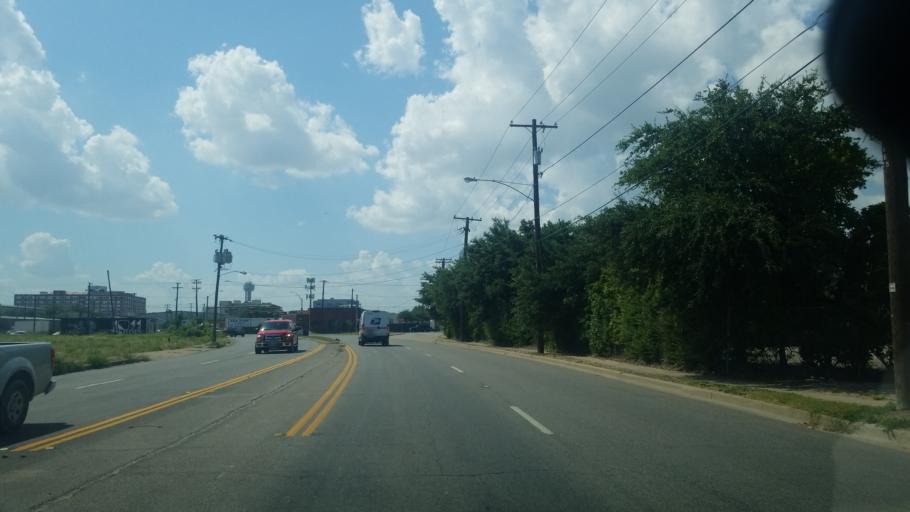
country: US
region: Texas
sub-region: Dallas County
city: Dallas
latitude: 32.7644
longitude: -96.7881
